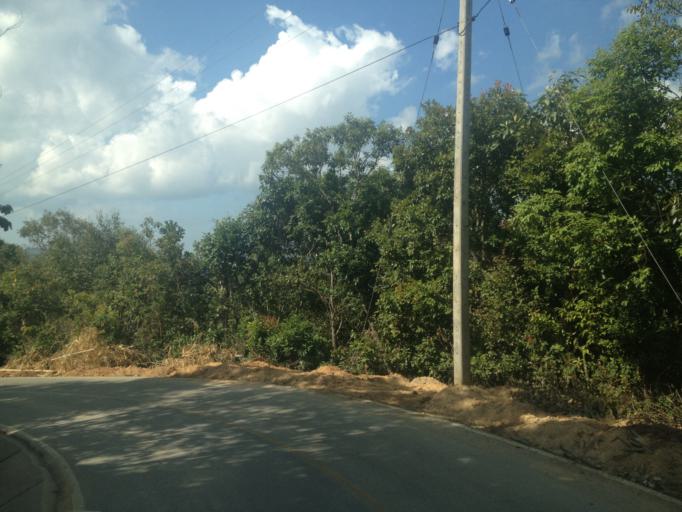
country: TH
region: Mae Hong Son
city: Ban Huai I Huak
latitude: 18.1313
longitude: 98.1443
